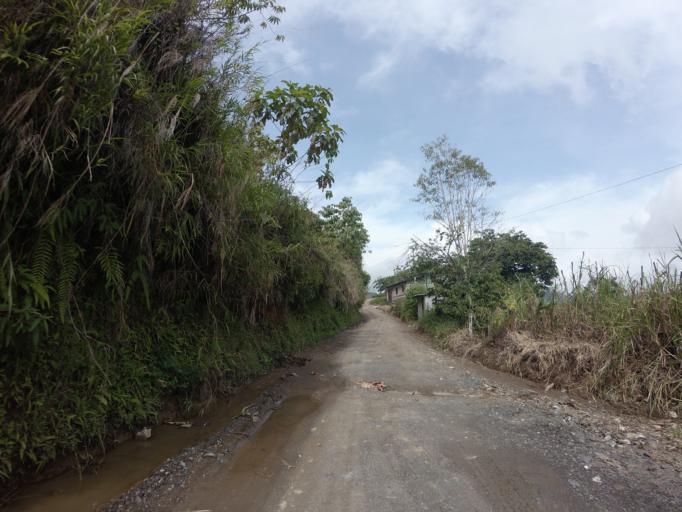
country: CO
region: Caldas
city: Marquetalia
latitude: 5.3426
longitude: -75.0431
